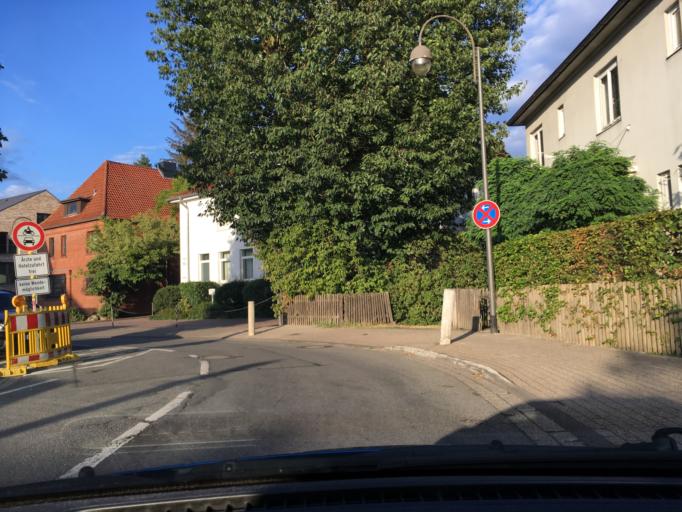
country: DE
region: Lower Saxony
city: Celle
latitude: 52.6226
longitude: 10.0850
